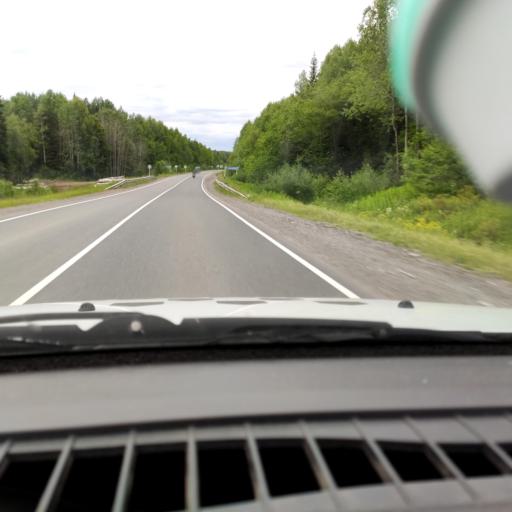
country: RU
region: Perm
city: Lys'va
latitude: 58.1880
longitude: 57.7934
